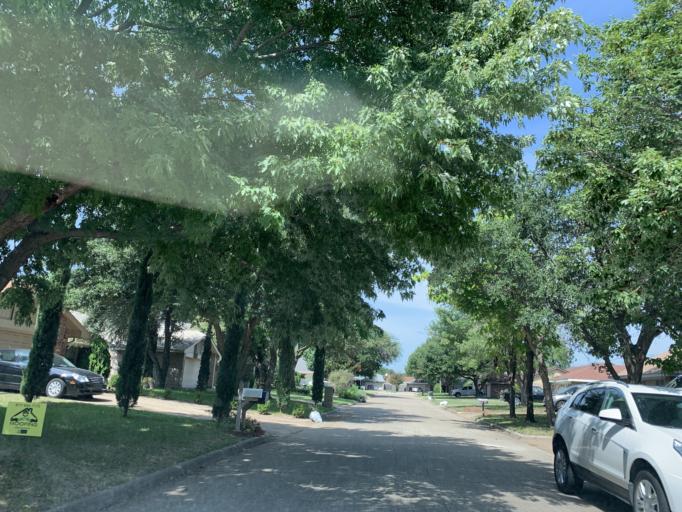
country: US
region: Texas
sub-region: Dallas County
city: Grand Prairie
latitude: 32.6701
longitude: -97.0423
